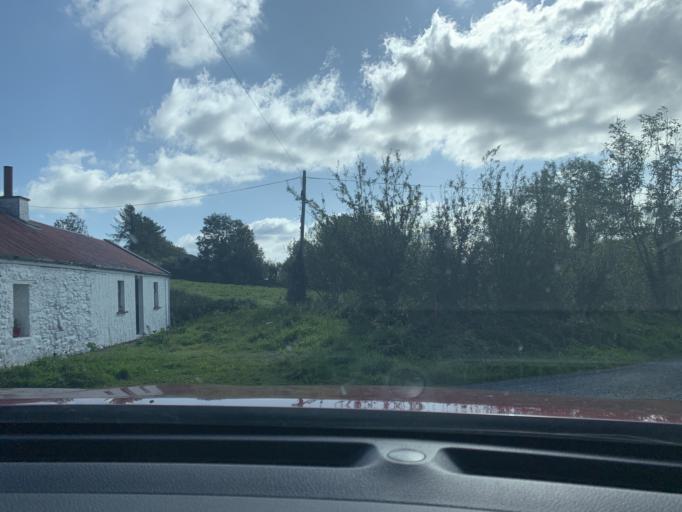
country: IE
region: Connaught
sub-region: Roscommon
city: Boyle
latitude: 54.0753
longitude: -8.3634
